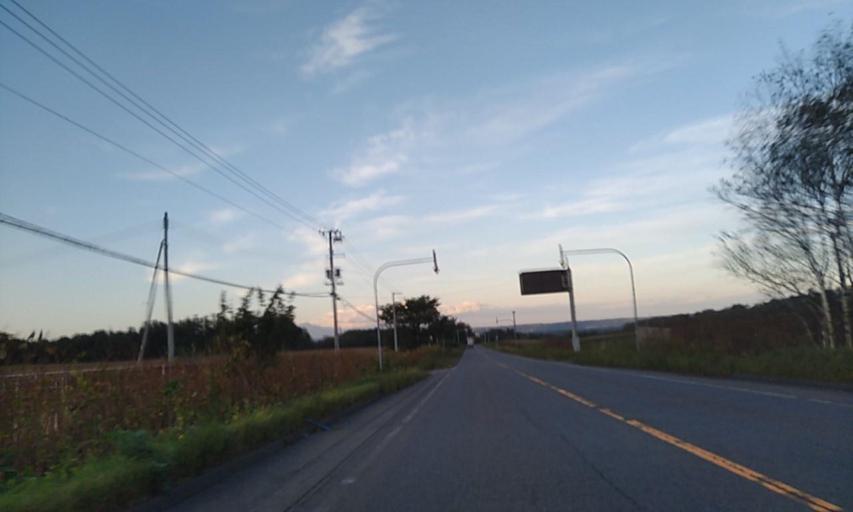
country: JP
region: Hokkaido
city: Otofuke
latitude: 42.9983
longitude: 142.8595
